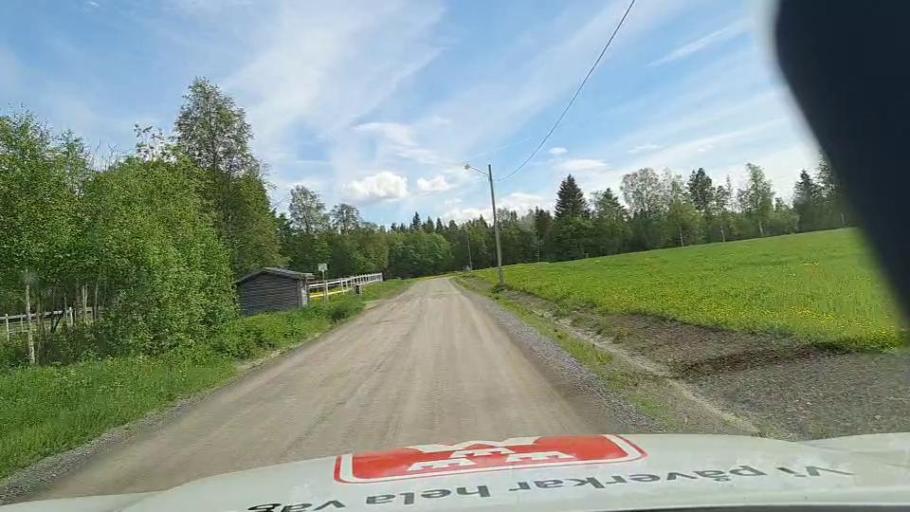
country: SE
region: Jaemtland
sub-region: OEstersunds Kommun
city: Brunflo
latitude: 63.0018
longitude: 14.8049
